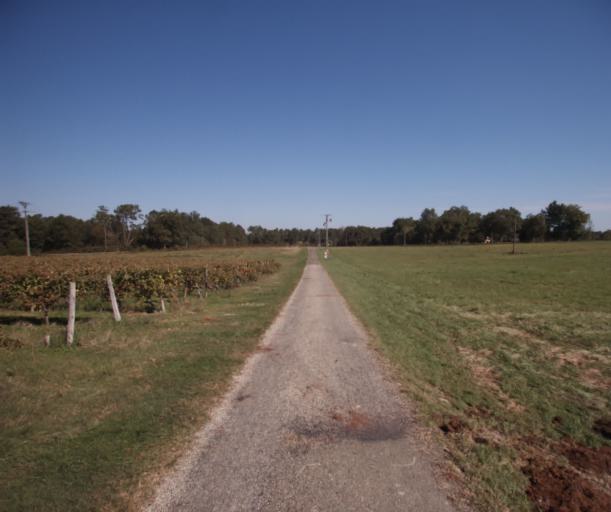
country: FR
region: Aquitaine
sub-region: Departement des Landes
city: Gabarret
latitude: 43.9506
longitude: -0.0061
